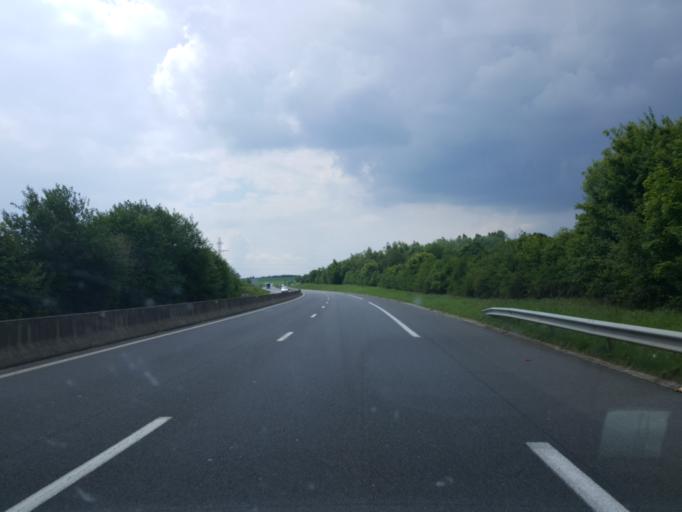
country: FR
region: Picardie
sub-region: Departement de l'Oise
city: Allonne
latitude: 49.3943
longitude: 2.1133
